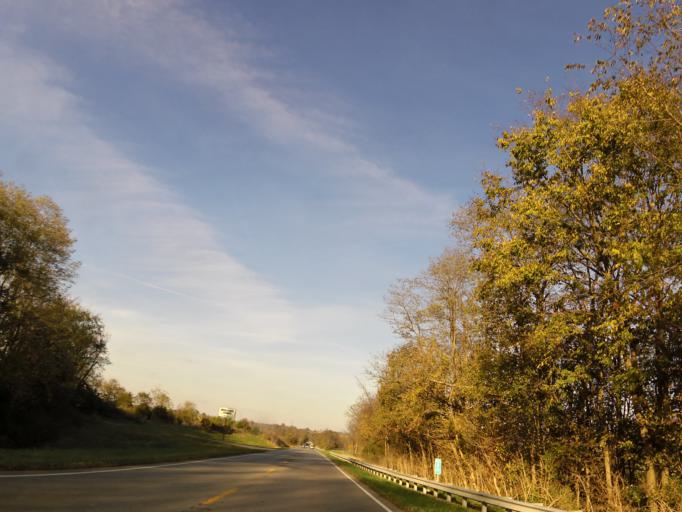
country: US
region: Kentucky
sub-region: Lincoln County
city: Stanford
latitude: 37.5600
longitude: -84.6268
